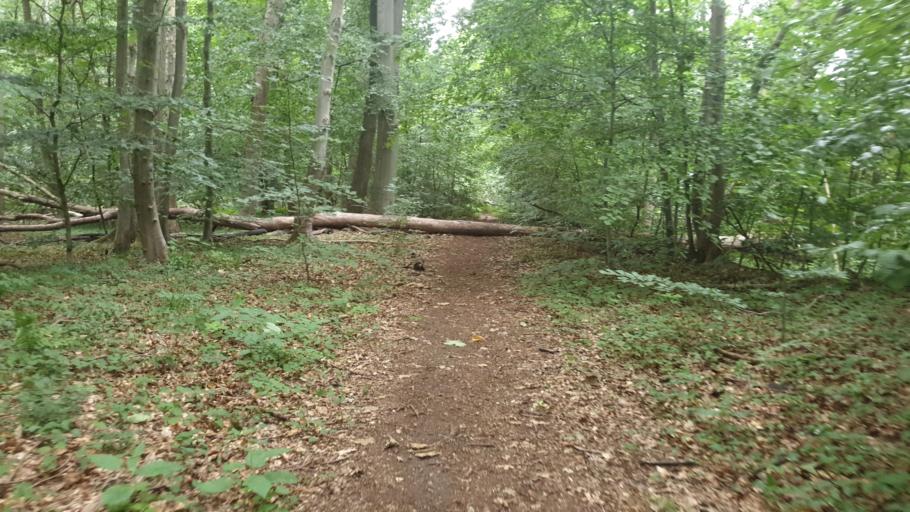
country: DE
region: Mecklenburg-Vorpommern
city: Werdervorstadt
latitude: 53.6454
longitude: 11.4528
